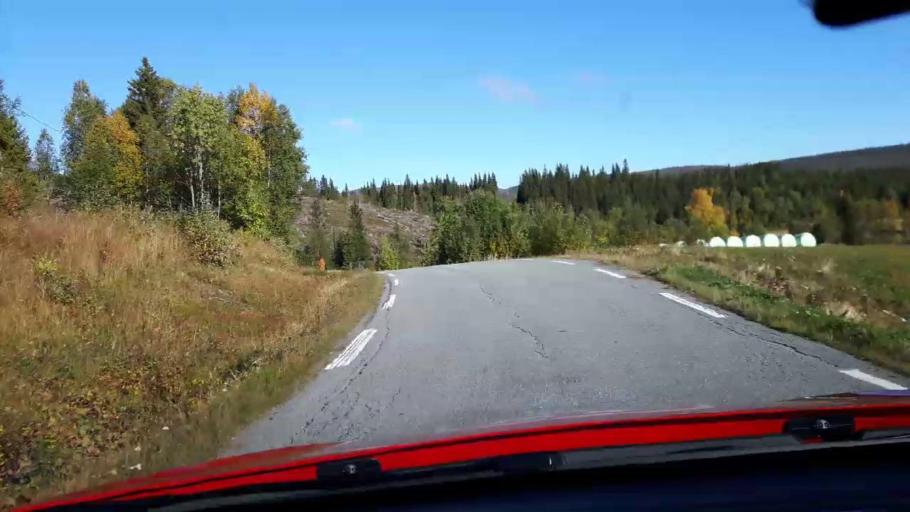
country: NO
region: Nord-Trondelag
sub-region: Lierne
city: Sandvika
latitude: 64.6353
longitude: 13.6969
